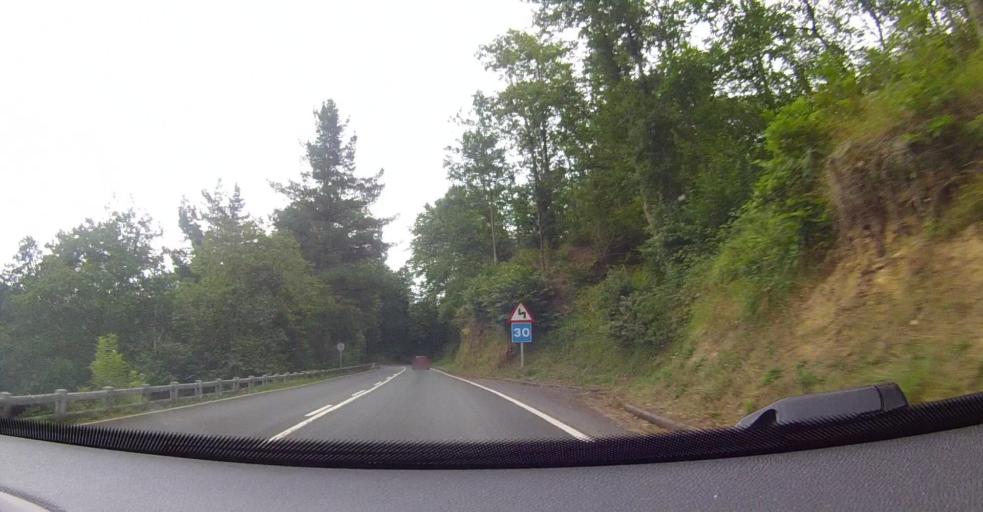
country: ES
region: Basque Country
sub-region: Bizkaia
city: Balmaseda
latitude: 43.2381
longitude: -3.2085
